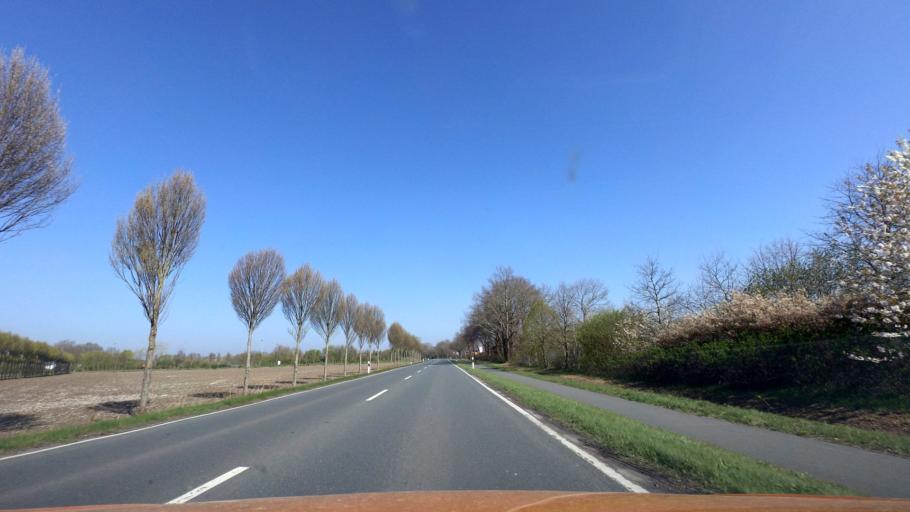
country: DE
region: Lower Saxony
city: Wardenburg
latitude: 53.0444
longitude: 8.2077
